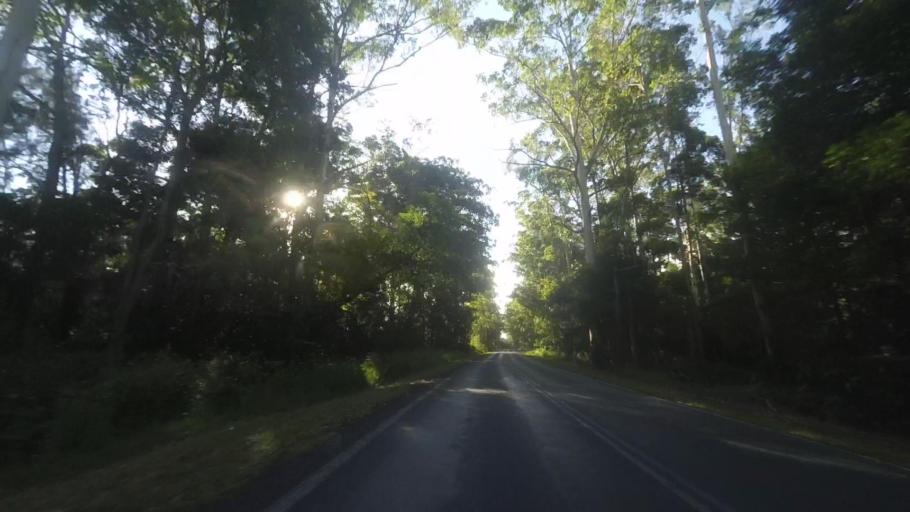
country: AU
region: New South Wales
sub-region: Great Lakes
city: Nabiac
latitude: -32.0915
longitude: 152.4381
